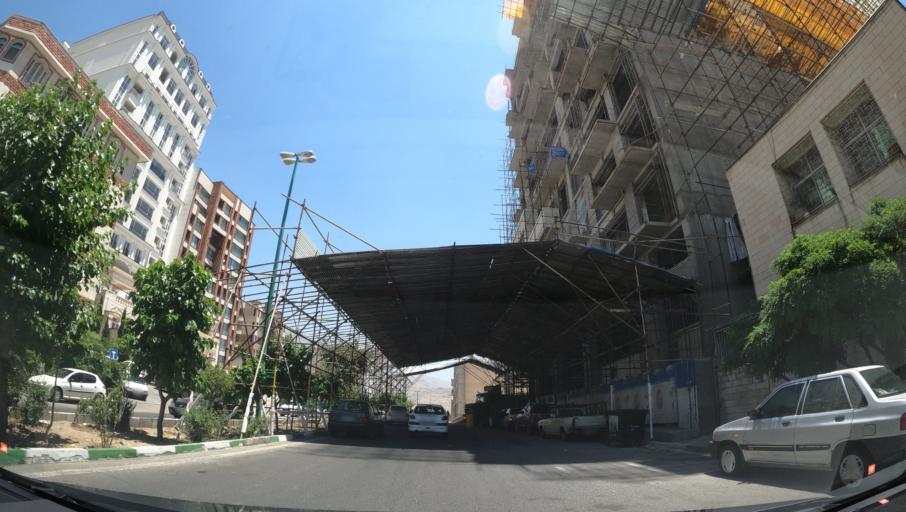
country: IR
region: Tehran
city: Tajrish
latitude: 35.8120
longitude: 51.3957
